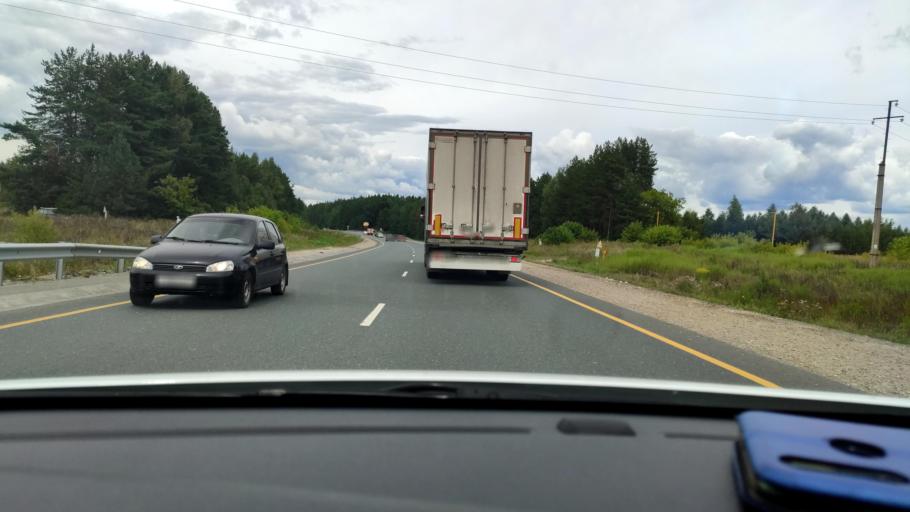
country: RU
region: Mariy-El
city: Pomary
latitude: 55.9975
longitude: 48.3825
